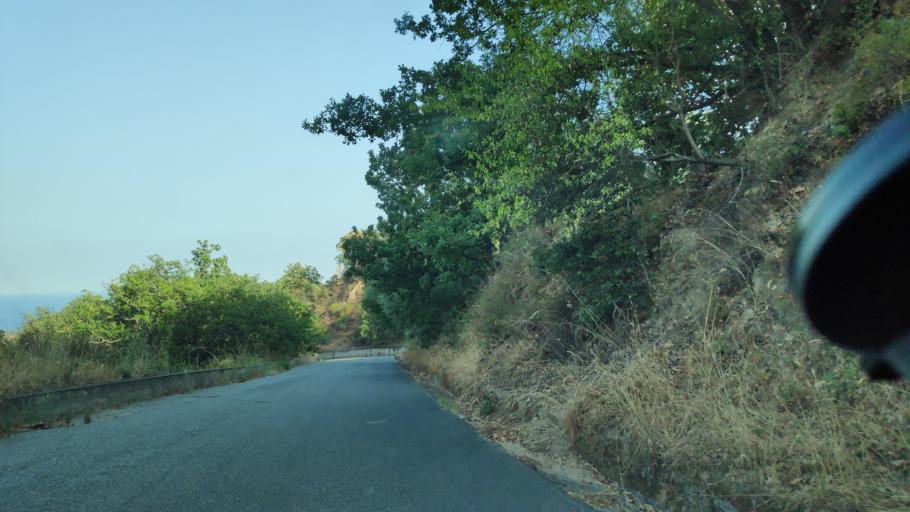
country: IT
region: Calabria
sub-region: Provincia di Catanzaro
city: Sant'Andrea Apostolo dello Ionio
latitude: 38.6178
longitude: 16.5314
